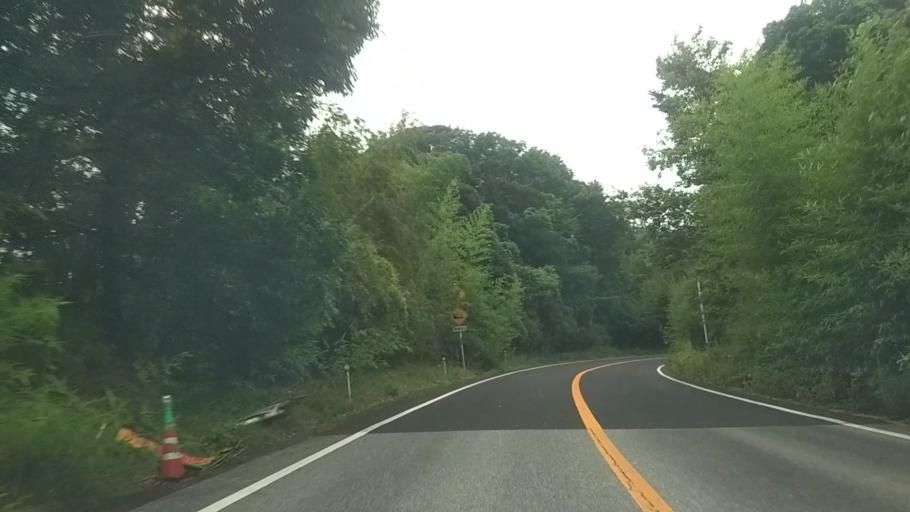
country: JP
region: Chiba
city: Kimitsu
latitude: 35.2438
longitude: 140.0057
